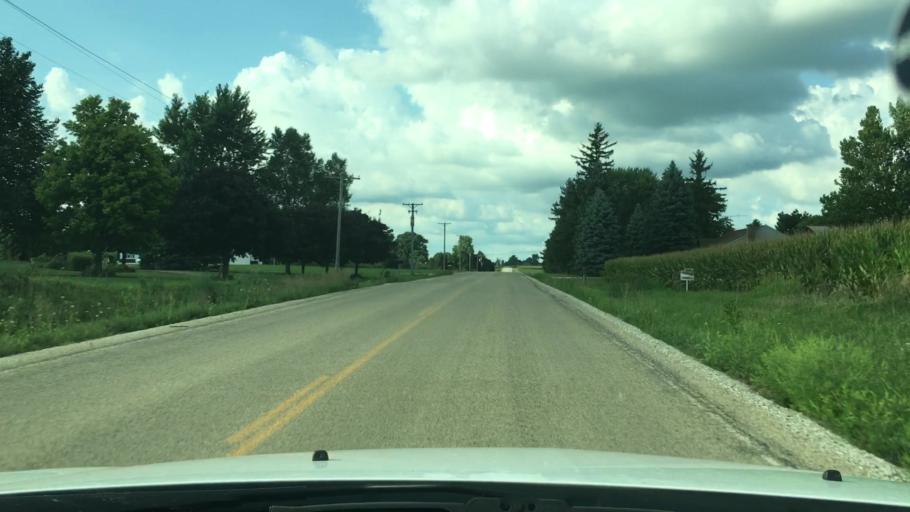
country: US
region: Illinois
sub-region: DeKalb County
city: Waterman
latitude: 41.7980
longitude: -88.7737
